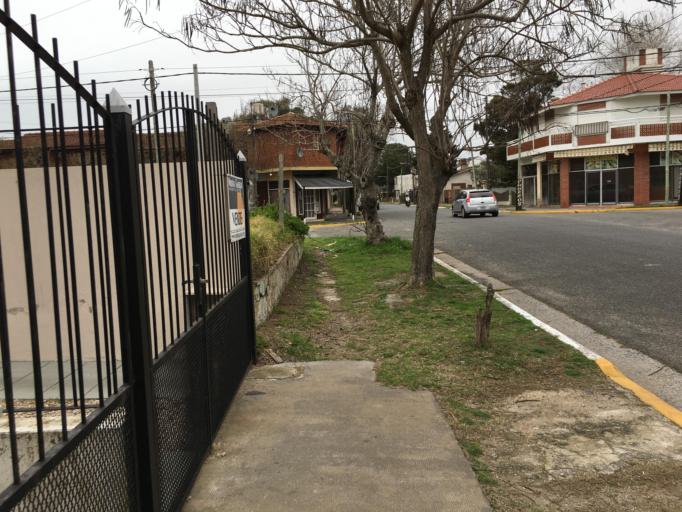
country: AR
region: Buenos Aires
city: Mar del Tuyu
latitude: -36.5556
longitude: -56.6913
